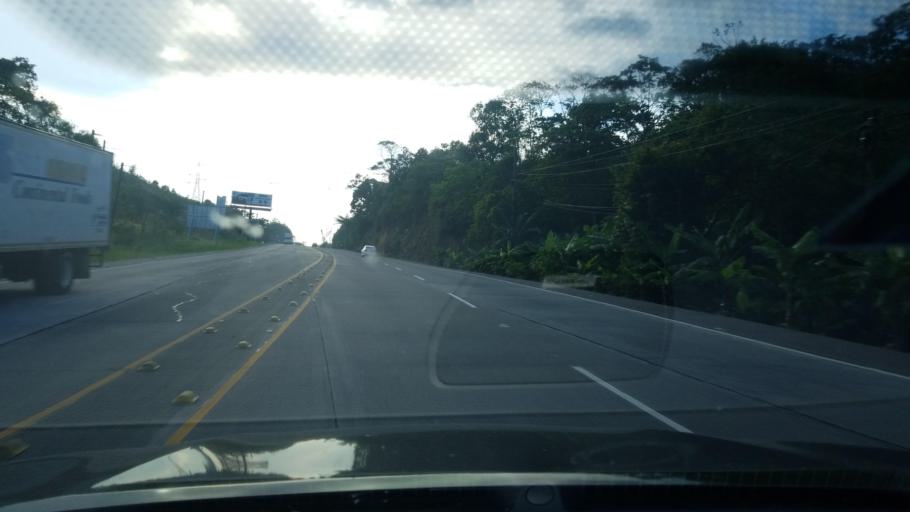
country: HN
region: Comayagua
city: El Socorro
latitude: 14.6592
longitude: -87.9442
